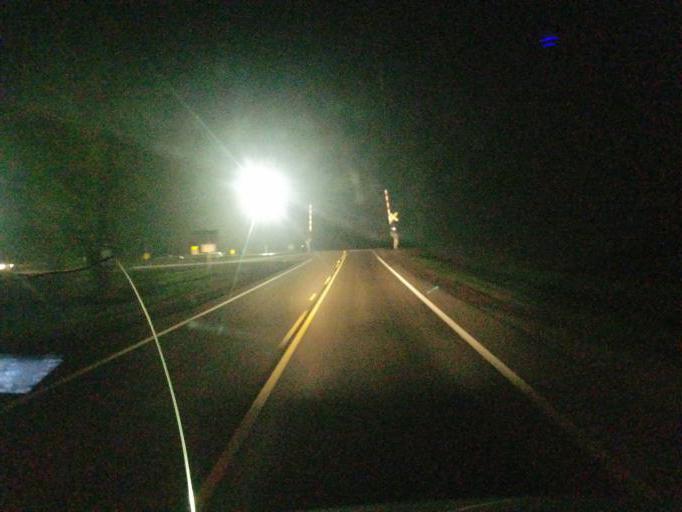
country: US
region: Ohio
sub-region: Huron County
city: Monroeville
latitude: 41.3030
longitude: -82.7361
